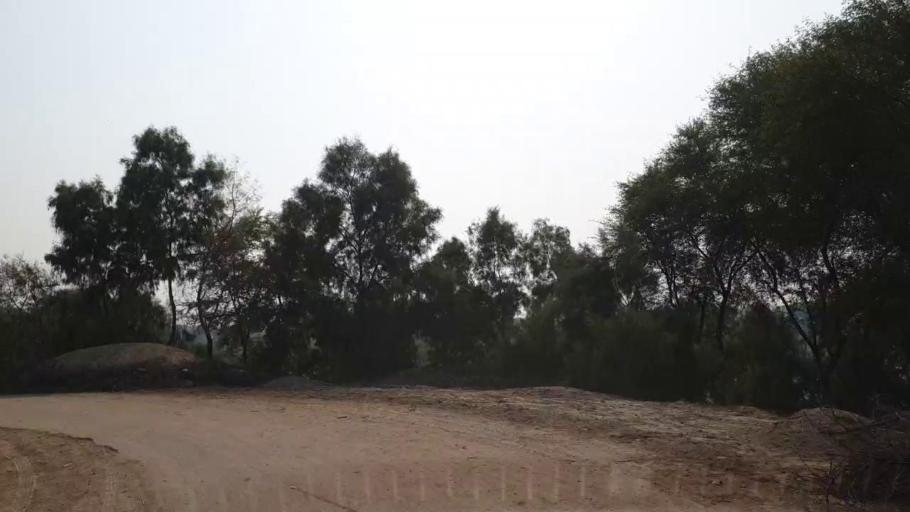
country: PK
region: Sindh
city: Bhan
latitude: 26.5177
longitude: 67.7378
